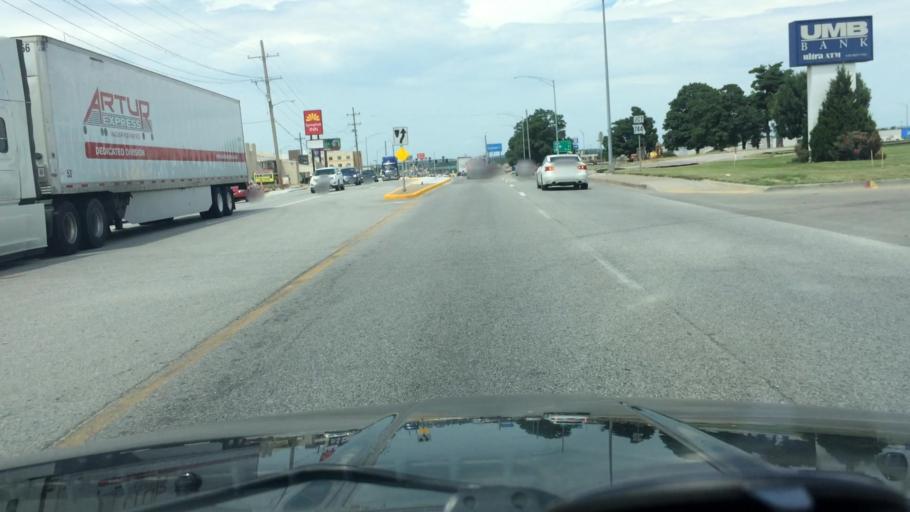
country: US
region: Missouri
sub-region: Greene County
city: Springfield
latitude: 37.2378
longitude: -93.2610
